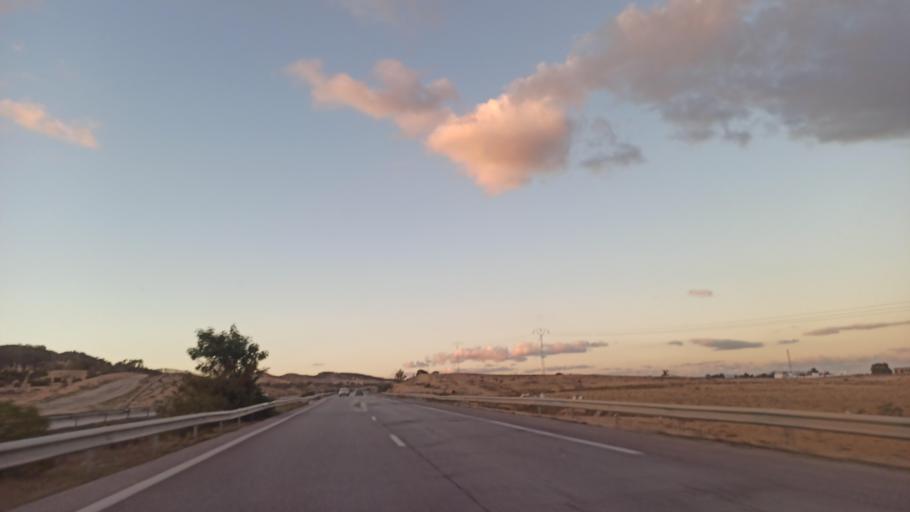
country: TN
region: Susah
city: Harqalah
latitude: 36.2257
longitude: 10.4151
